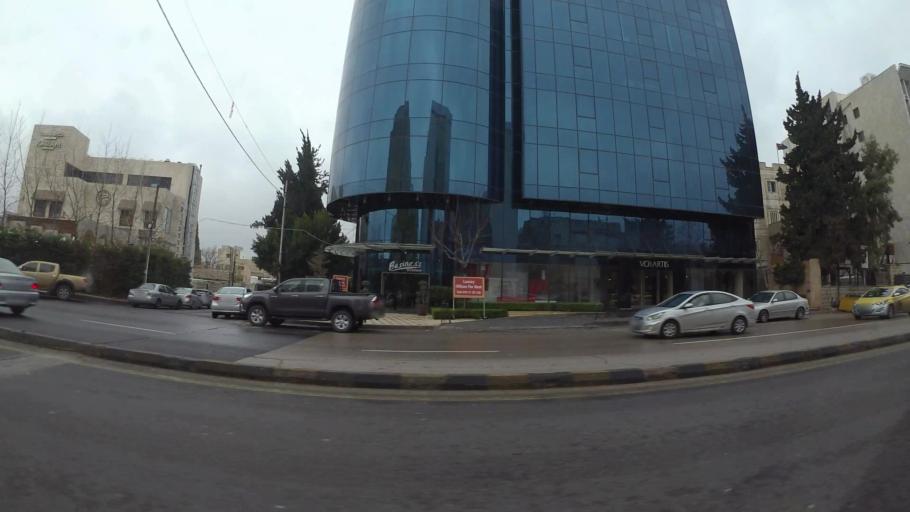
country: JO
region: Amman
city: Amman
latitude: 31.9532
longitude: 35.9126
